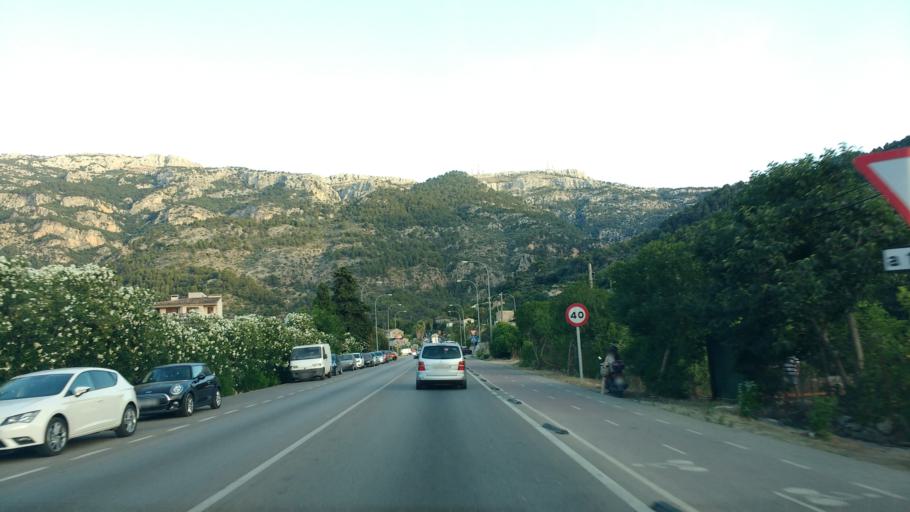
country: ES
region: Balearic Islands
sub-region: Illes Balears
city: Soller
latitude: 39.7681
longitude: 2.7074
